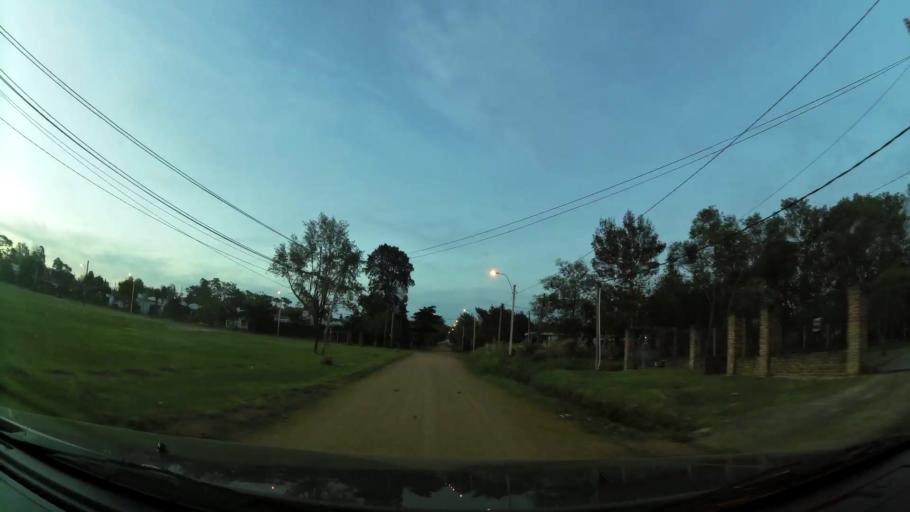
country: UY
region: Canelones
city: Atlantida
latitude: -34.7743
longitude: -55.7488
